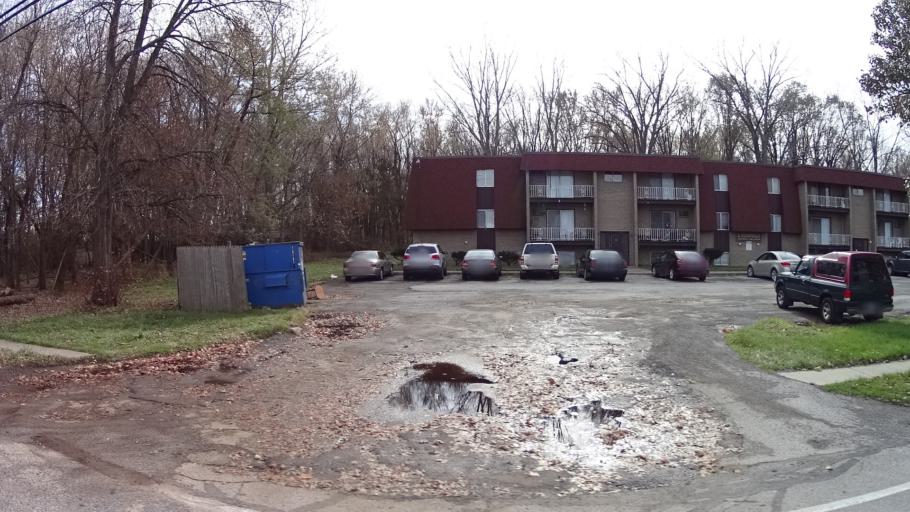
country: US
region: Ohio
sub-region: Lorain County
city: Sheffield Lake
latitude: 41.4976
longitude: -82.0776
